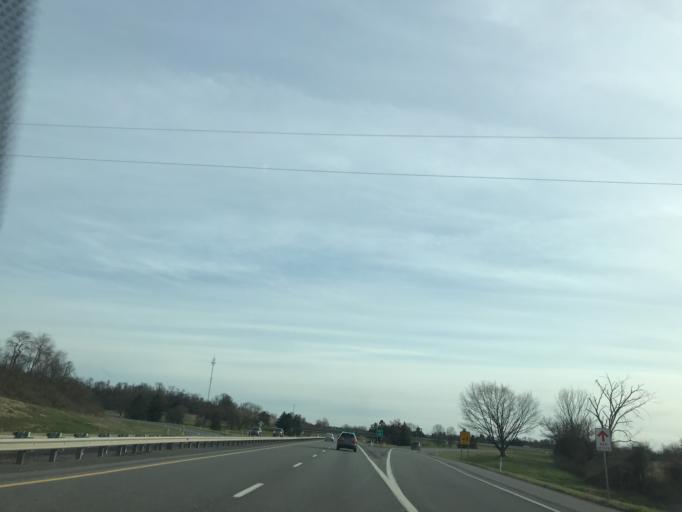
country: US
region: Pennsylvania
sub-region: Union County
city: New Columbia
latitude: 41.0543
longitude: -76.8384
